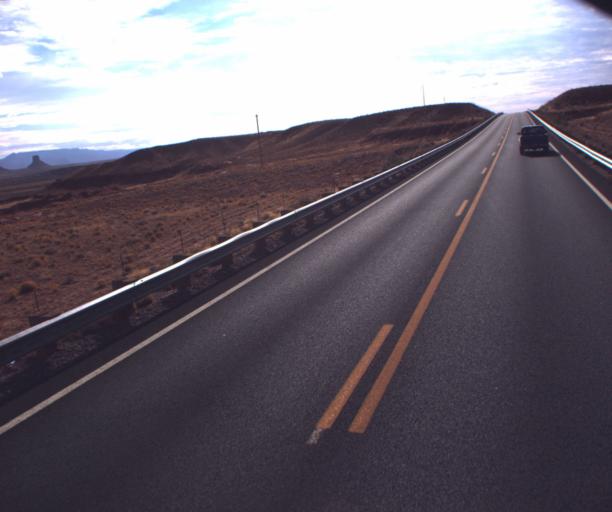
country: US
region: Arizona
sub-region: Apache County
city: Many Farms
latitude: 36.6028
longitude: -109.5710
